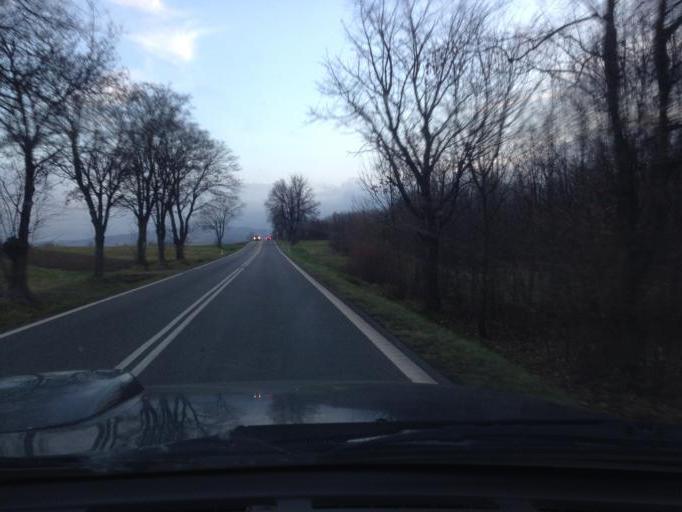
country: PL
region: Subcarpathian Voivodeship
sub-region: Powiat jasielski
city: Nowy Zmigrod
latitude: 49.6280
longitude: 21.5326
